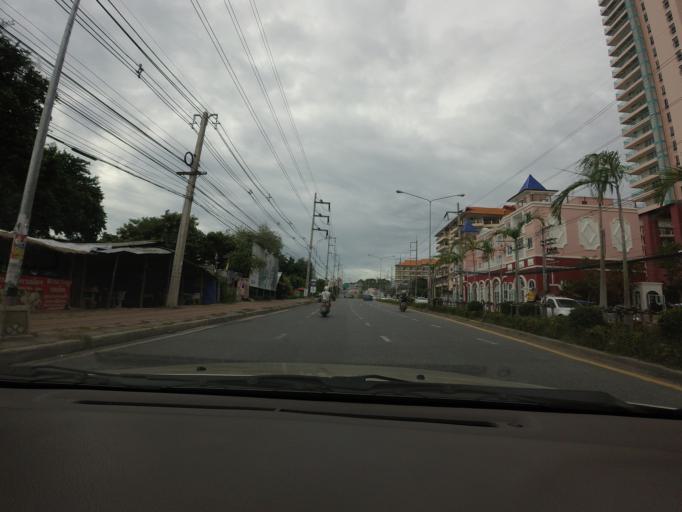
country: TH
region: Chon Buri
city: Phatthaya
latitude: 12.9074
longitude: 100.8688
